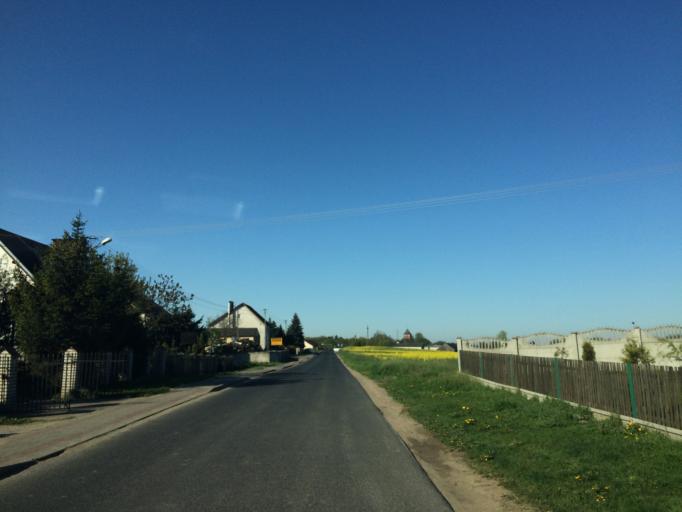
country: PL
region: Warmian-Masurian Voivodeship
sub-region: Powiat ilawski
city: Lubawa
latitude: 53.4168
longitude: 19.7682
